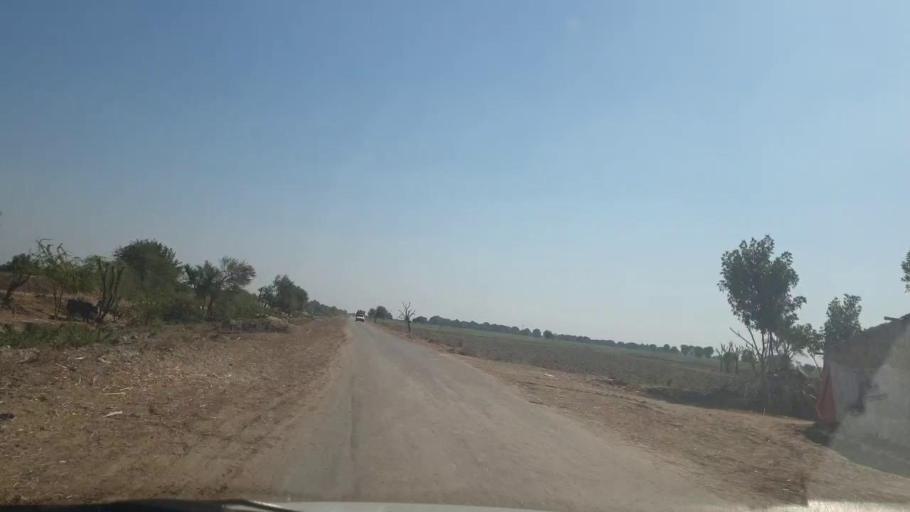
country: PK
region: Sindh
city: Mirpur Khas
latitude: 25.4692
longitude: 69.1772
